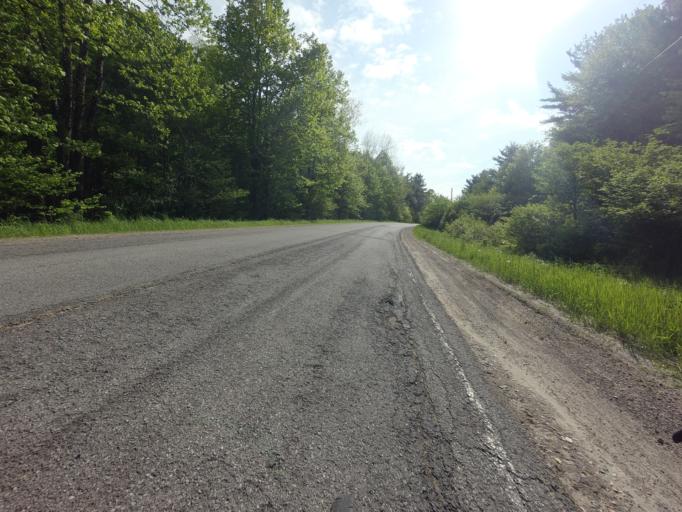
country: US
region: New York
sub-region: St. Lawrence County
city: Gouverneur
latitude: 44.2617
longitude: -75.2125
